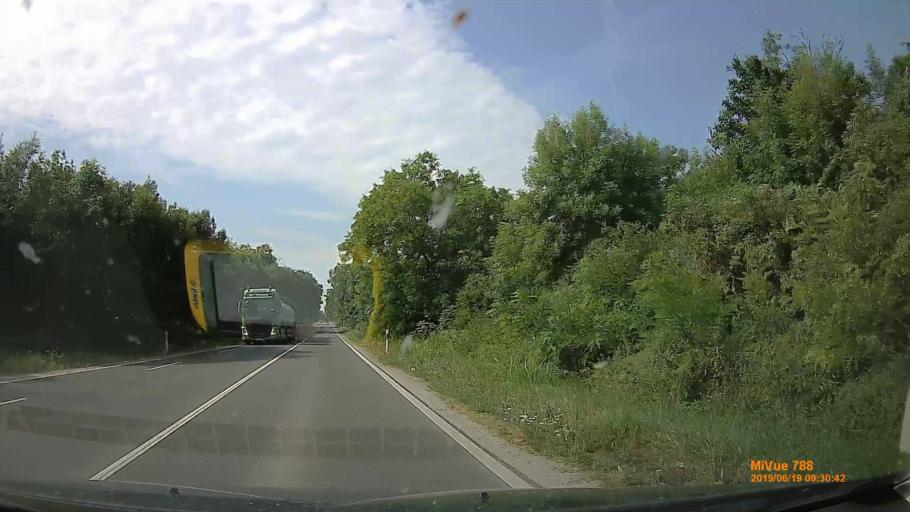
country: HU
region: Pest
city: Szazhalombatta
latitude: 47.3157
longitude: 18.8898
